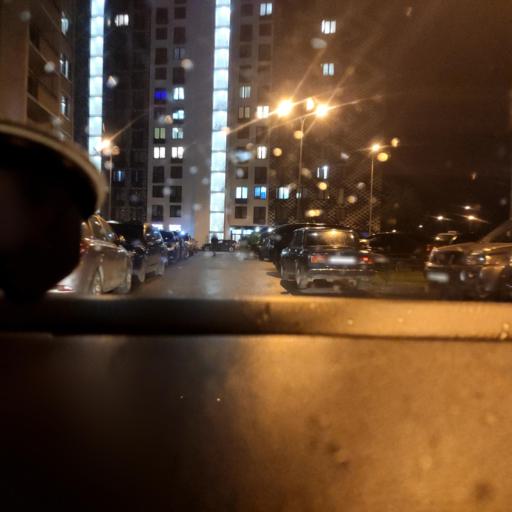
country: RU
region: Moskovskaya
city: Vidnoye
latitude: 55.5331
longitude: 37.7224
